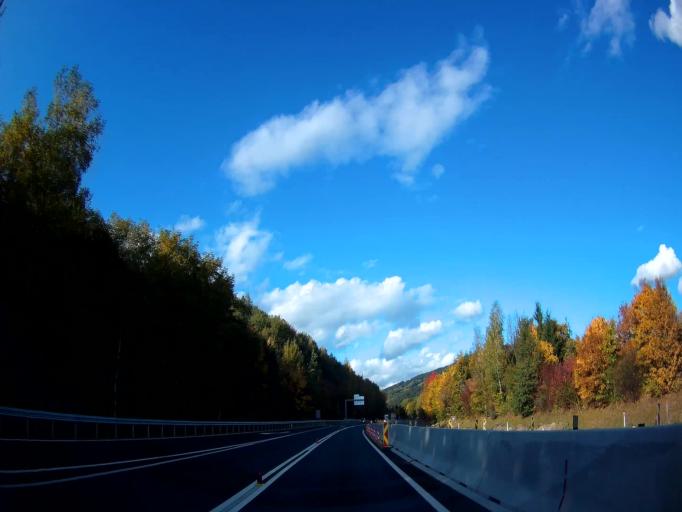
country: AT
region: Carinthia
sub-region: Politischer Bezirk Wolfsberg
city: Wolfsberg
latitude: 46.8509
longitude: 14.8353
